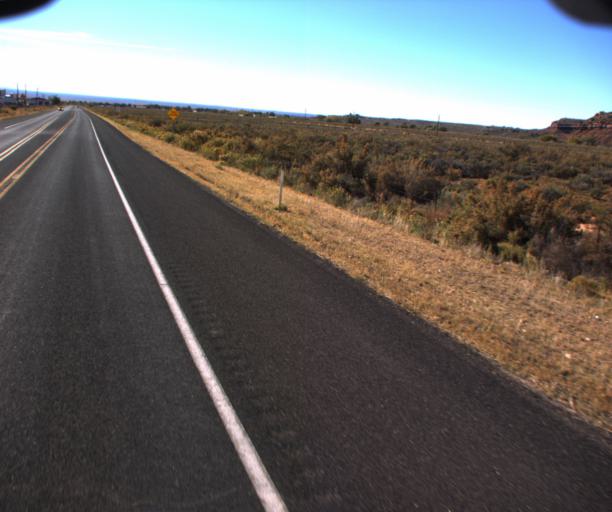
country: US
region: Arizona
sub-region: Coconino County
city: Fredonia
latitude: 36.9764
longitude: -112.5285
